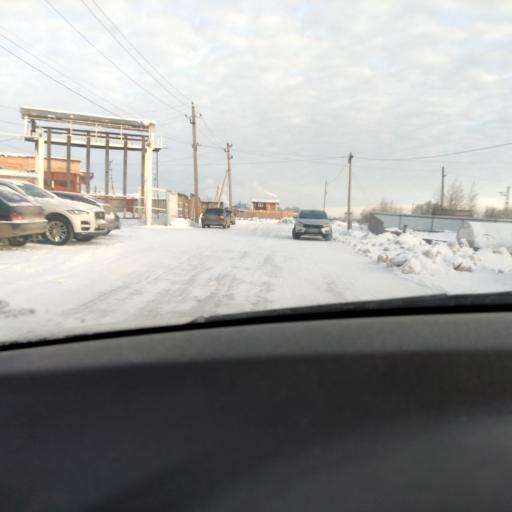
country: RU
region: Perm
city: Bershet'
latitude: 57.8106
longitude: 56.3762
